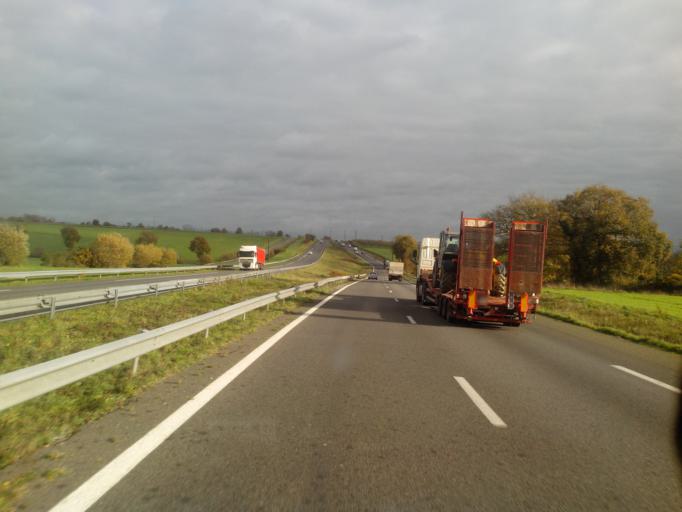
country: FR
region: Brittany
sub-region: Departement d'Ille-et-Vilaine
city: Bedee
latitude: 48.1860
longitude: -1.9829
